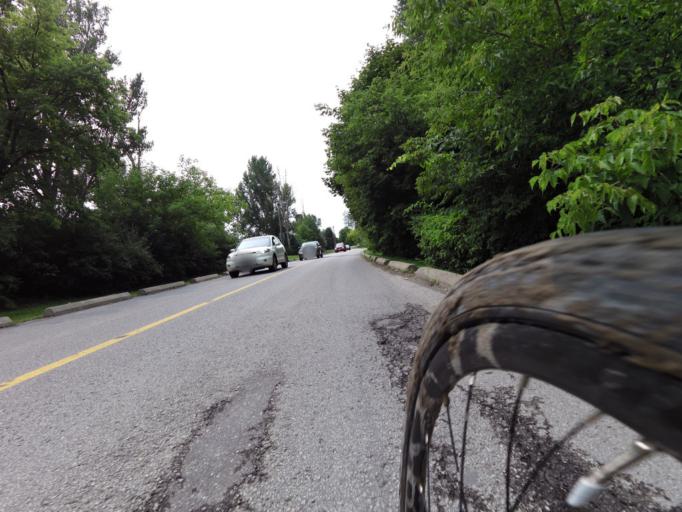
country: CA
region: Ontario
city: Scarborough
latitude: 43.7100
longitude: -79.2328
